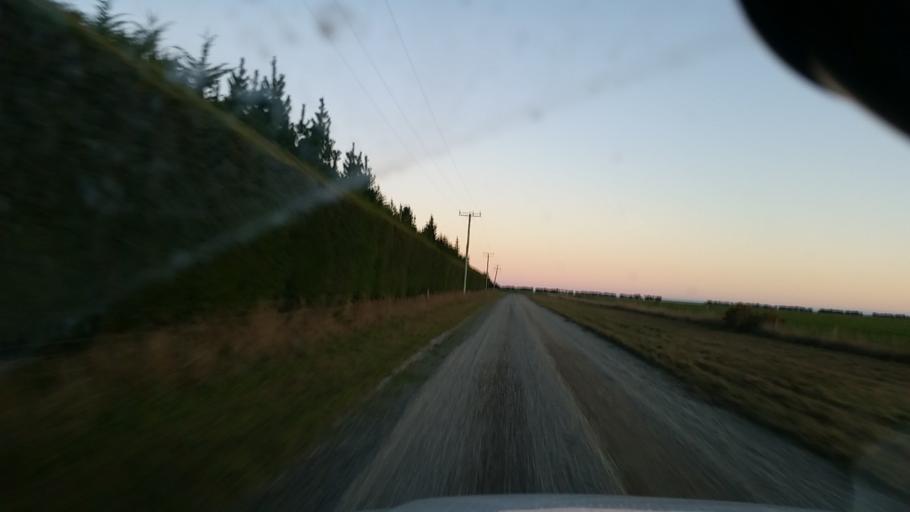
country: NZ
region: Canterbury
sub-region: Ashburton District
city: Tinwald
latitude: -44.0851
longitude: 171.6664
